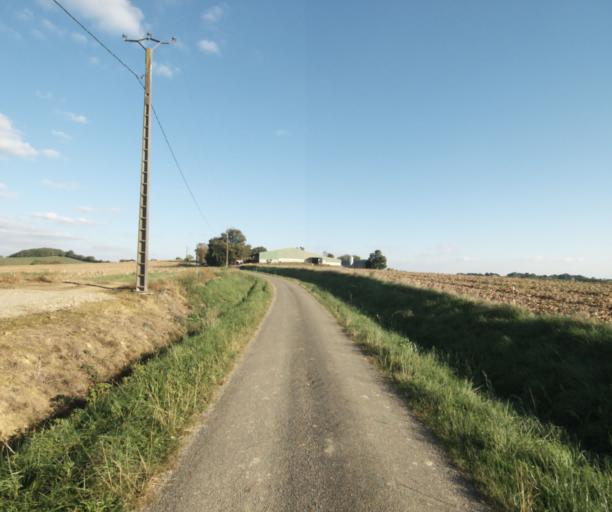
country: FR
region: Midi-Pyrenees
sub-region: Departement du Gers
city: Eauze
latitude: 43.7631
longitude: 0.1033
